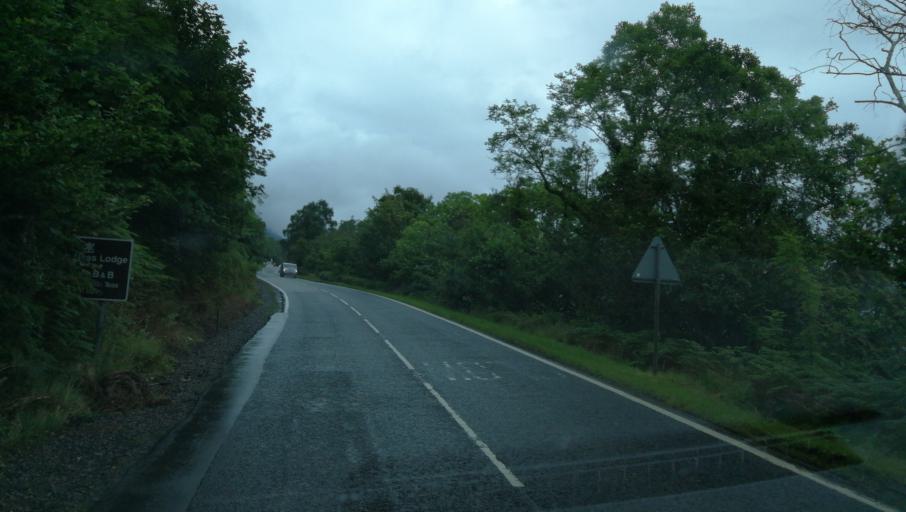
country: GB
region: Scotland
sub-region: Highland
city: Beauly
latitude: 57.3616
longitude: -4.3954
